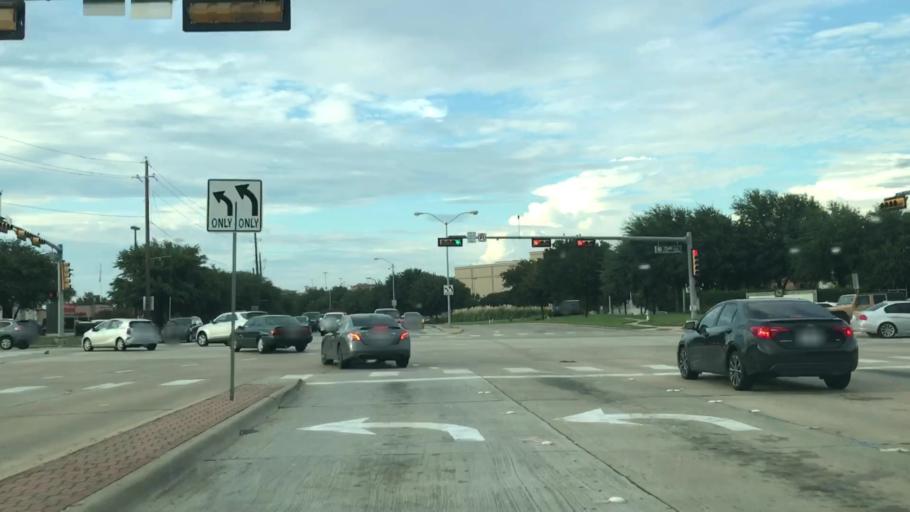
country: US
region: Texas
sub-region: Dallas County
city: Addison
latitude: 33.0273
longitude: -96.8351
